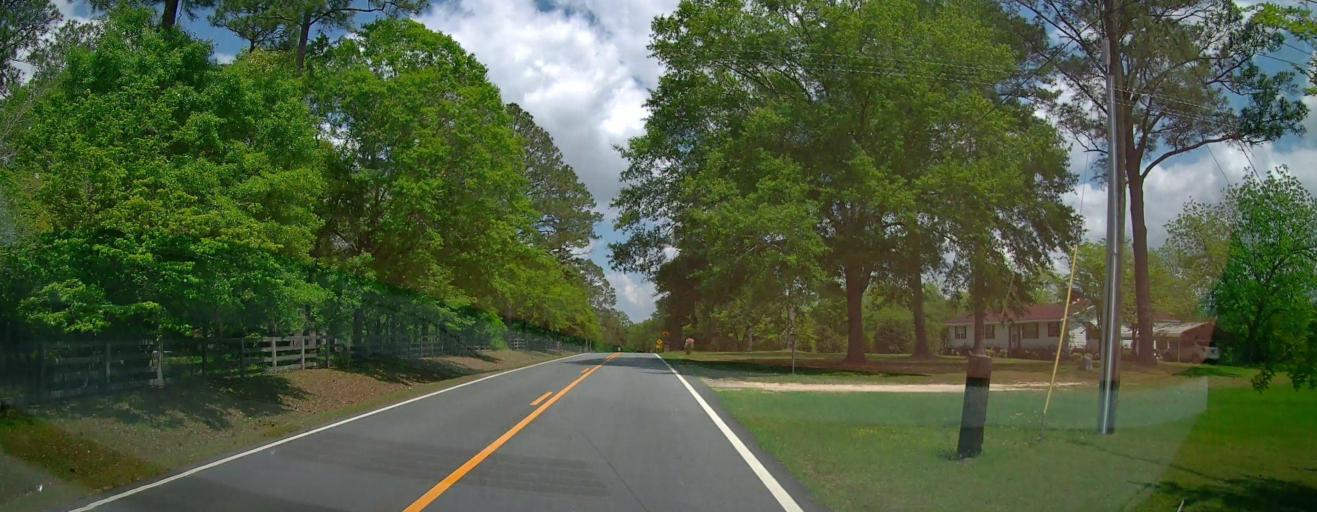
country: US
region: Georgia
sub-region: Laurens County
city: East Dublin
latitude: 32.6058
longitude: -82.8986
